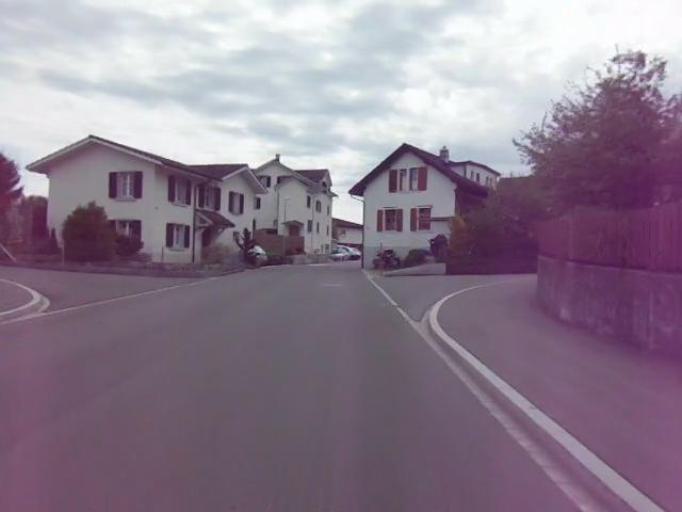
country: CH
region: Zurich
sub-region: Bezirk Hinwil
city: Rueti / Westlicher Dorfteil
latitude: 47.2564
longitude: 8.8441
